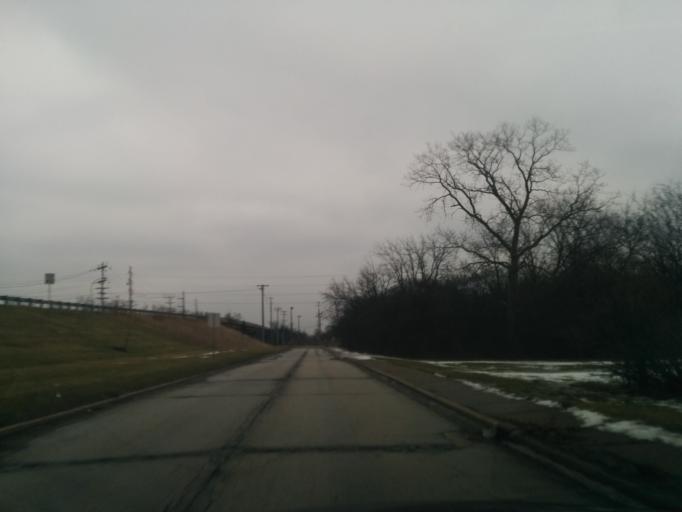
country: US
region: Illinois
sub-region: Cook County
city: Westchester
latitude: 41.8487
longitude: -87.8689
